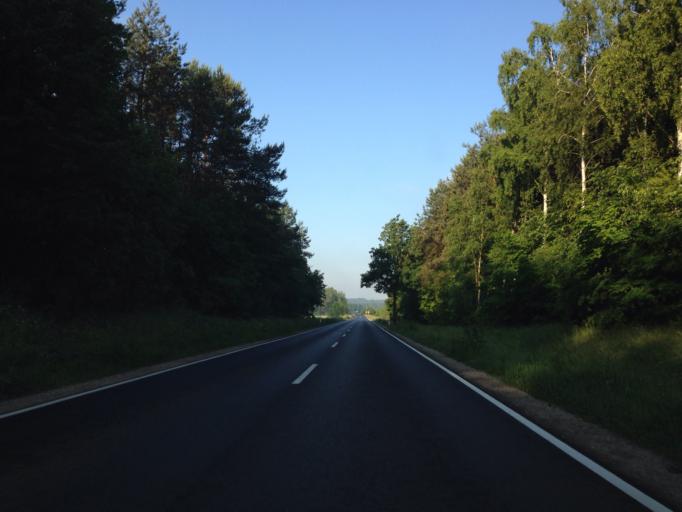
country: PL
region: Kujawsko-Pomorskie
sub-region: Grudziadz
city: Grudziadz
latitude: 53.5369
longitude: 18.8288
